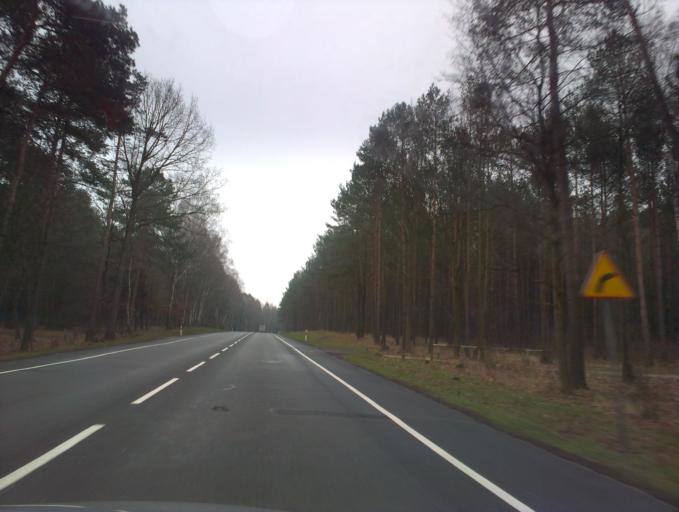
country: PL
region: Greater Poland Voivodeship
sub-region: Powiat chodzieski
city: Chodziez
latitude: 53.0178
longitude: 16.8307
